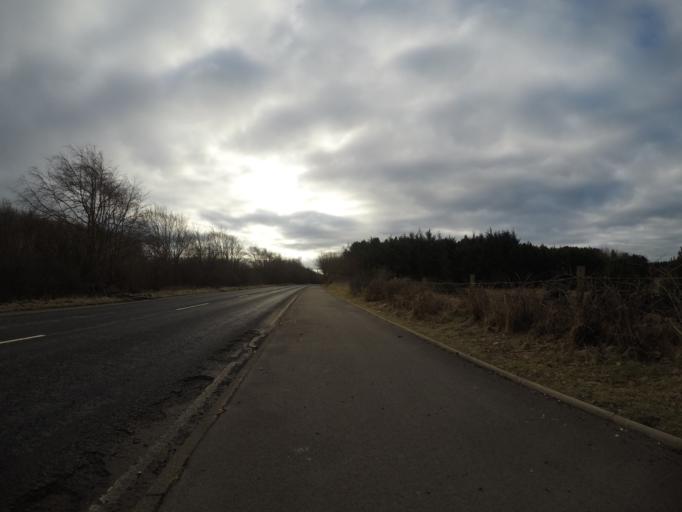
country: GB
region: Scotland
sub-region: North Ayrshire
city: Irvine
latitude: 55.5919
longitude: -4.6522
